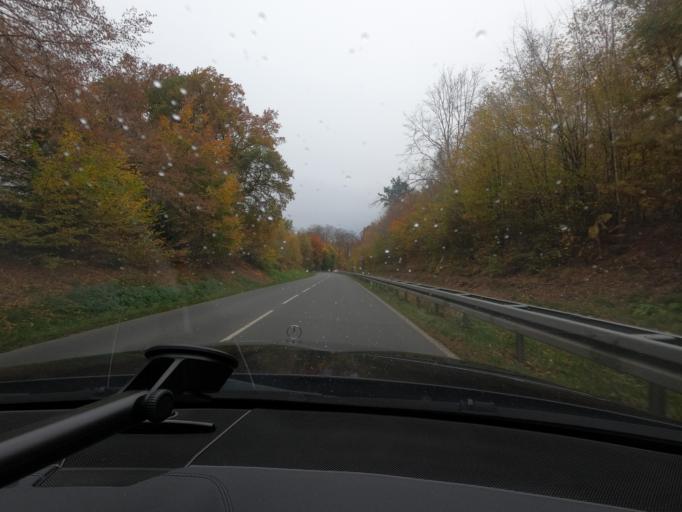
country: DE
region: North Rhine-Westphalia
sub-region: Regierungsbezirk Arnsberg
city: Mohnesee
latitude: 51.4802
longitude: 8.0880
